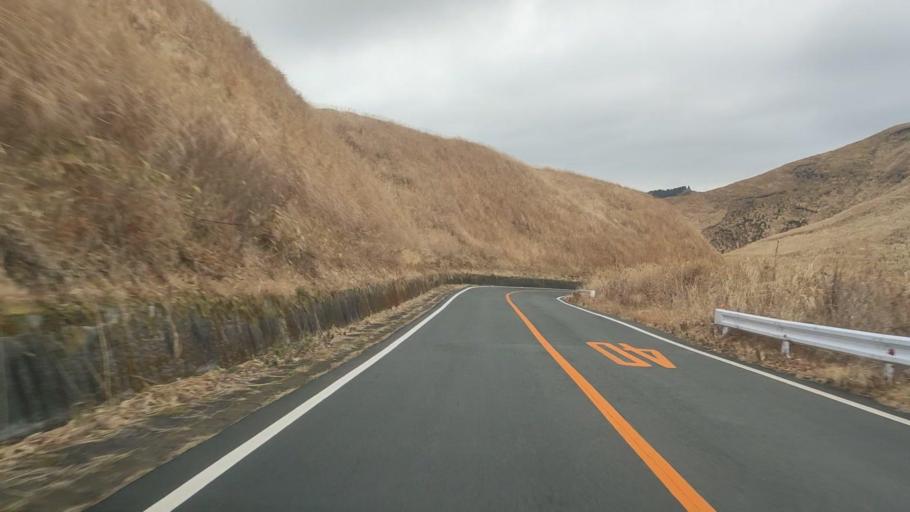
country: JP
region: Kumamoto
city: Aso
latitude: 32.9027
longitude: 131.1516
